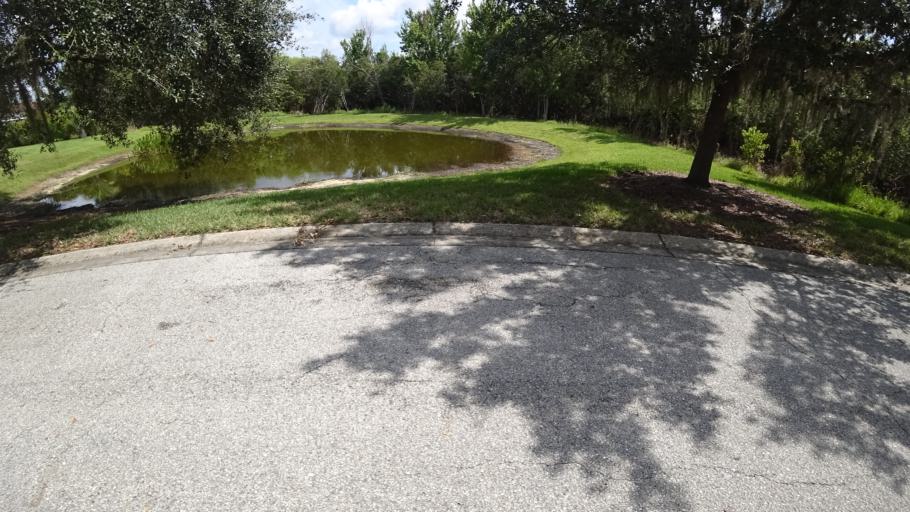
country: US
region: Florida
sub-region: Sarasota County
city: The Meadows
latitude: 27.4109
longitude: -82.4252
